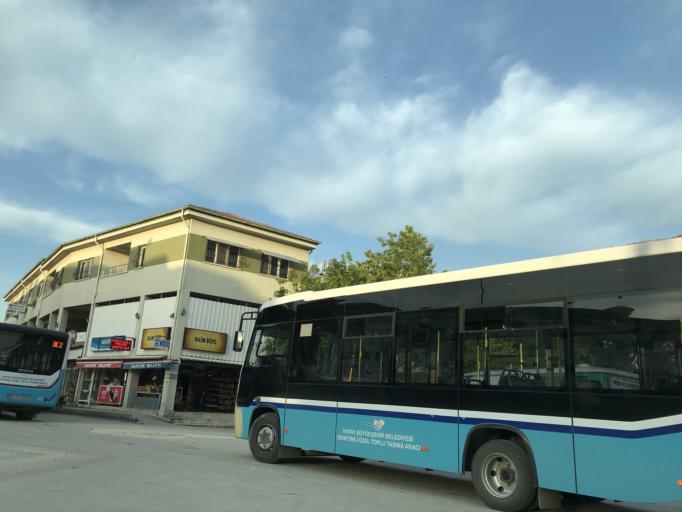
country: TR
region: Hatay
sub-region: Antakya Ilcesi
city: Antakya
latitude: 36.2125
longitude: 36.1657
